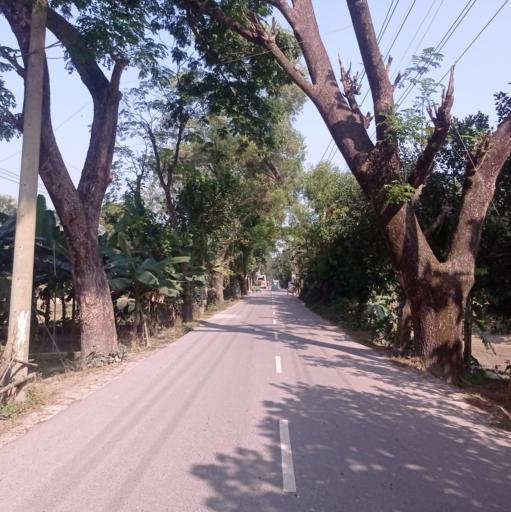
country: BD
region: Dhaka
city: Narsingdi
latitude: 24.0565
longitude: 90.6853
